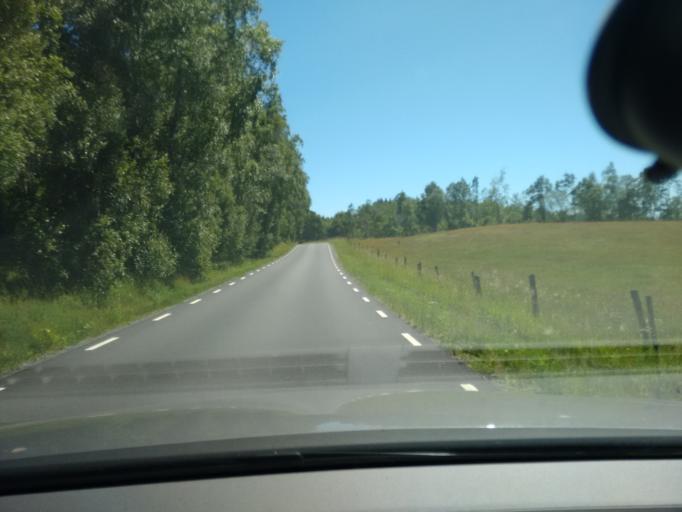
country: SE
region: Skane
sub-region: Kristianstads Kommun
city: Degeberga
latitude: 55.7746
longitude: 14.1250
